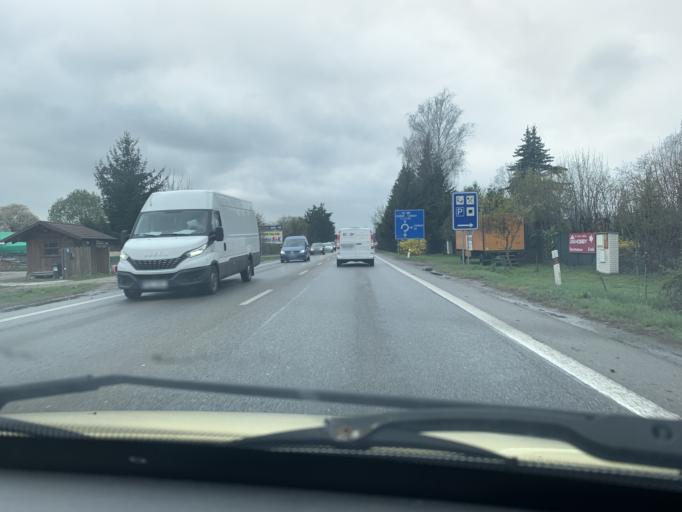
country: CZ
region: Jihocesky
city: Litvinovice
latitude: 48.9652
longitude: 14.4606
